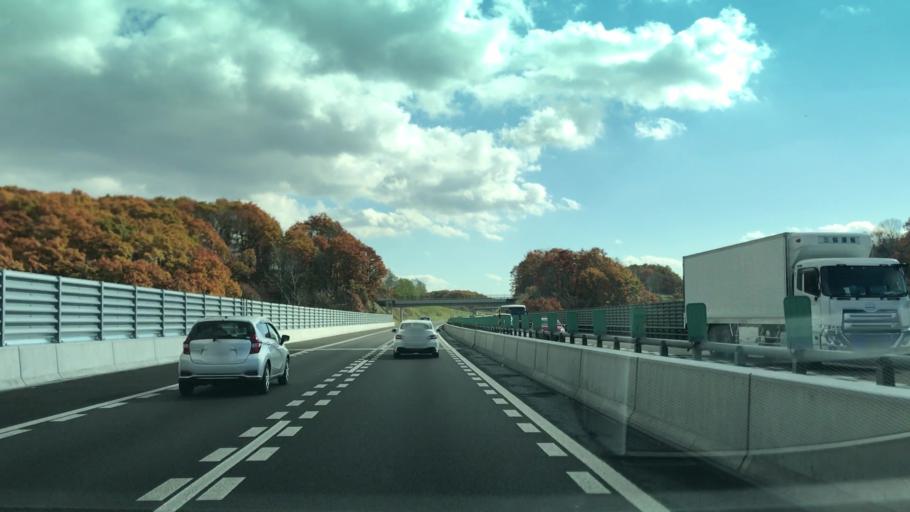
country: JP
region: Hokkaido
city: Kitahiroshima
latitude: 42.9238
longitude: 141.5410
